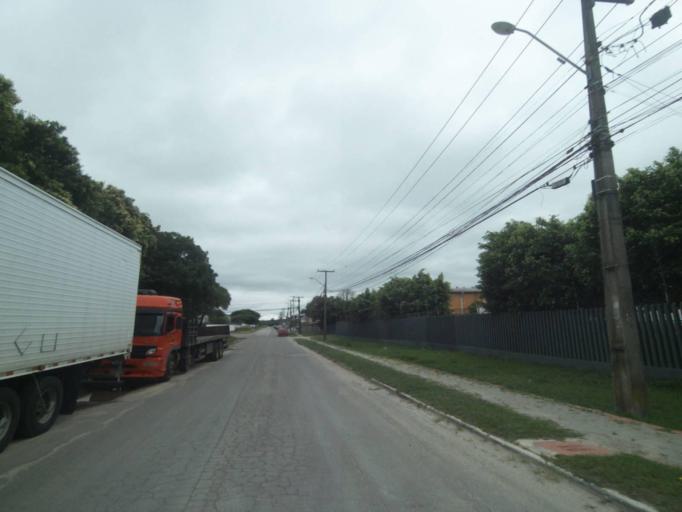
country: BR
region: Parana
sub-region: Curitiba
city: Curitiba
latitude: -25.5212
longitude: -49.3268
